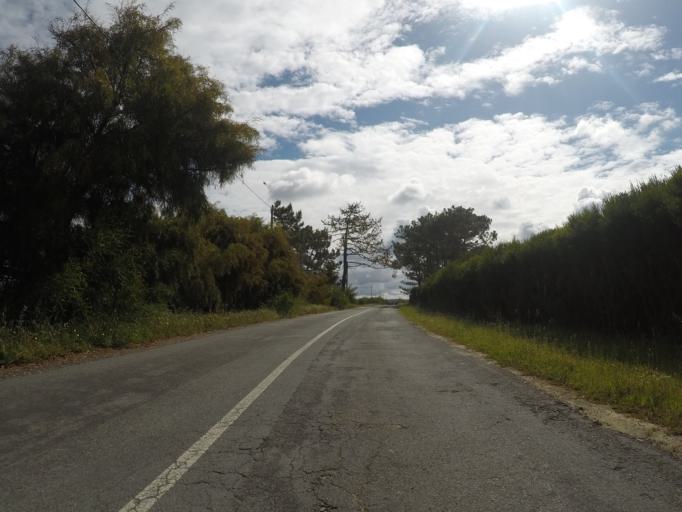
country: PT
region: Beja
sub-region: Odemira
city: Sao Teotonio
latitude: 37.4782
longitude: -8.7850
